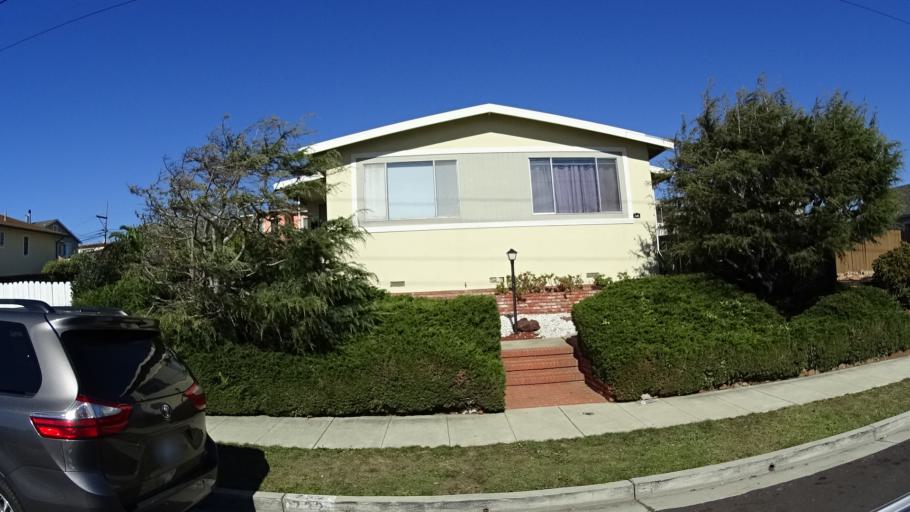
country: US
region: California
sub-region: San Mateo County
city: South San Francisco
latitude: 37.6564
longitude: -122.4251
